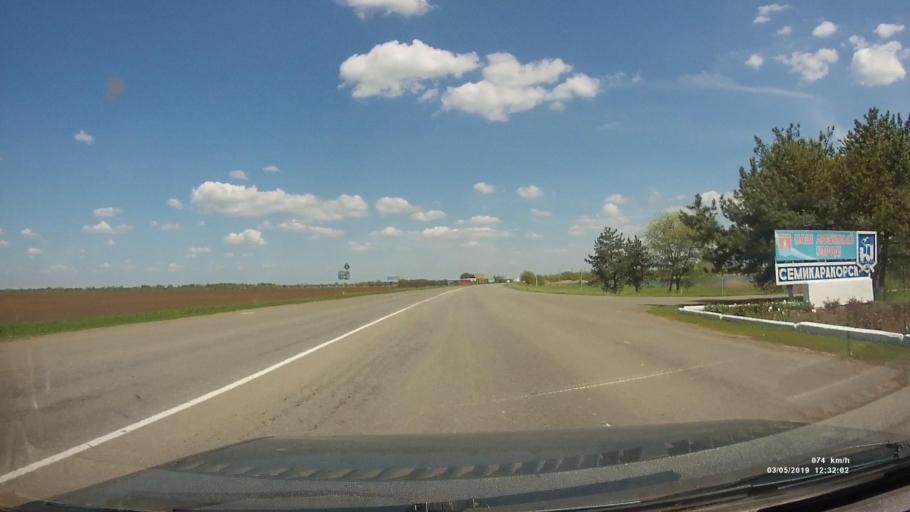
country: RU
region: Rostov
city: Semikarakorsk
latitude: 47.5092
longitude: 40.7538
